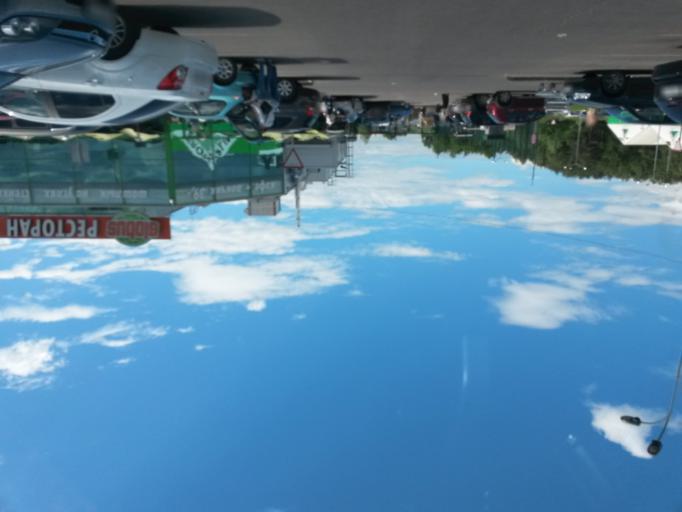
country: RU
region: Moskovskaya
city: Klimovsk
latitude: 55.3870
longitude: 37.5462
